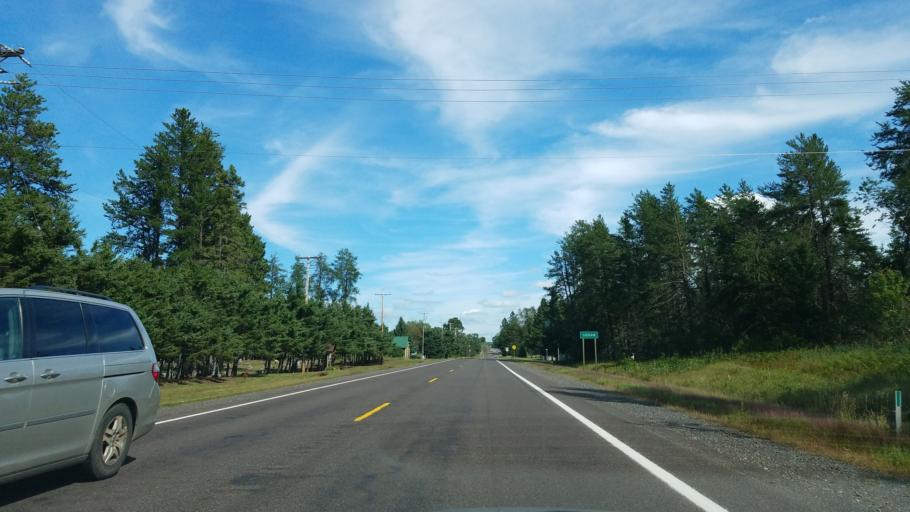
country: US
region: Michigan
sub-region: Baraga County
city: Baraga
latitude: 46.5066
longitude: -88.7217
